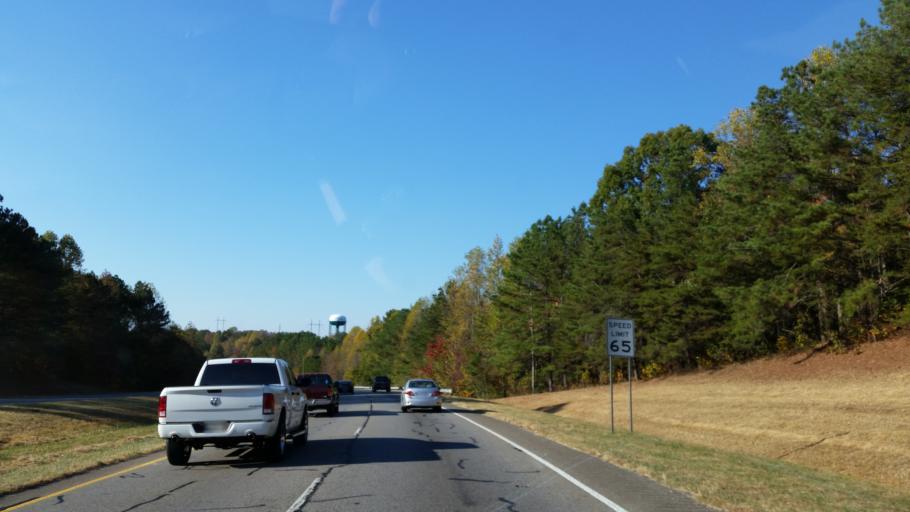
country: US
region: Georgia
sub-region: Pickens County
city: Jasper
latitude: 34.4828
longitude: -84.4682
